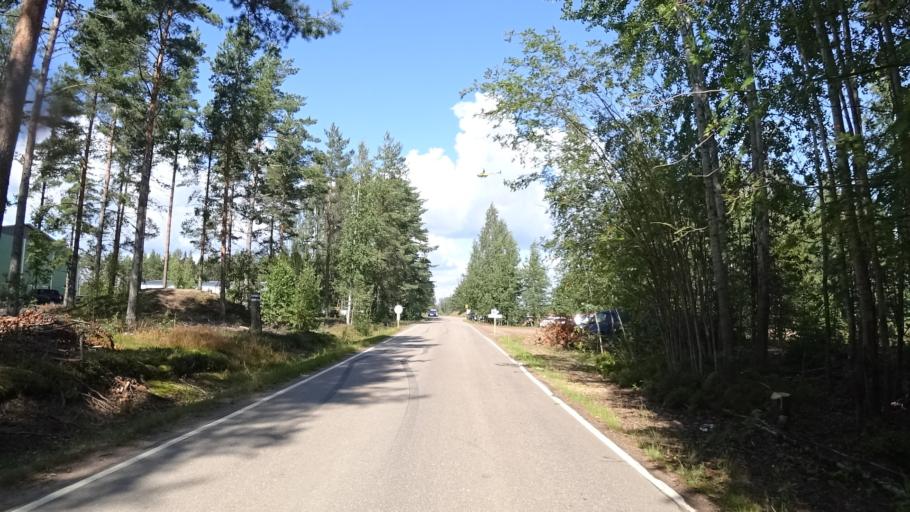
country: FI
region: Kymenlaakso
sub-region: Kotka-Hamina
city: Karhula
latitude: 60.5766
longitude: 26.8977
